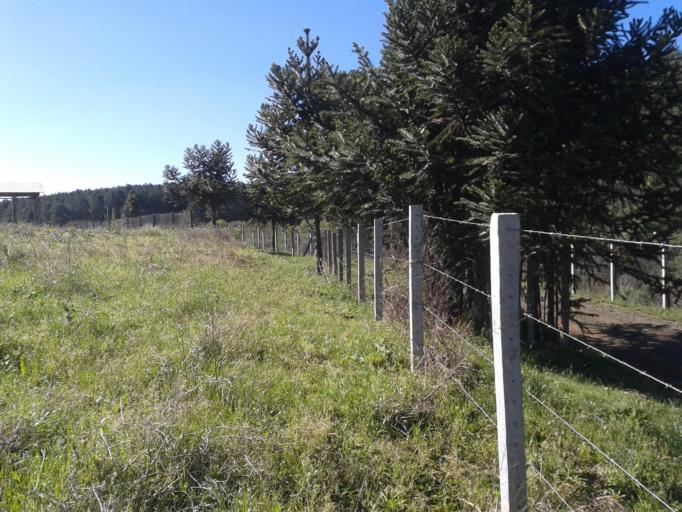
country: BR
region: Santa Catarina
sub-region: Curitibanos
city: Curitibanos
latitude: -27.2744
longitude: -50.5026
